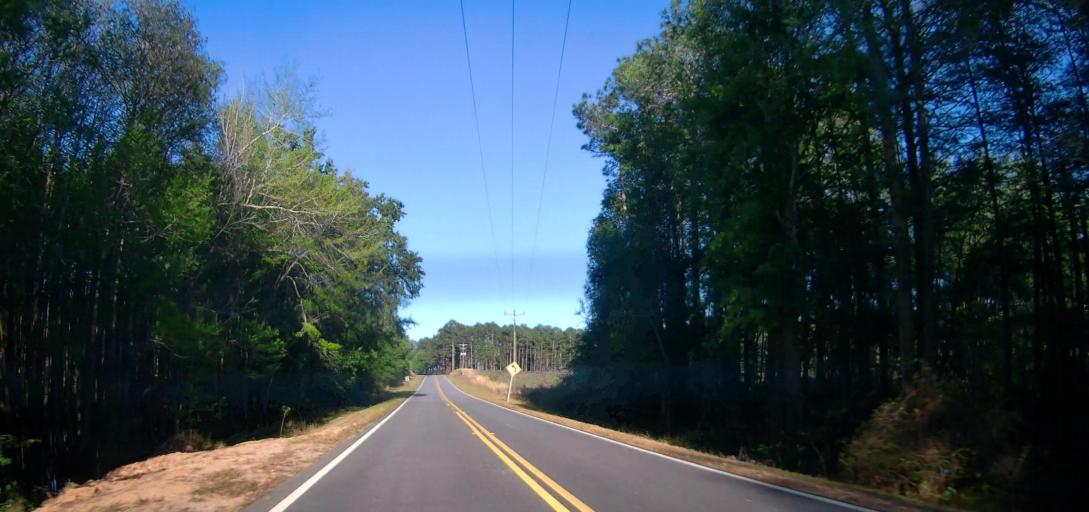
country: US
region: Georgia
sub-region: Ben Hill County
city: Fitzgerald
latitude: 31.6588
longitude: -83.1500
